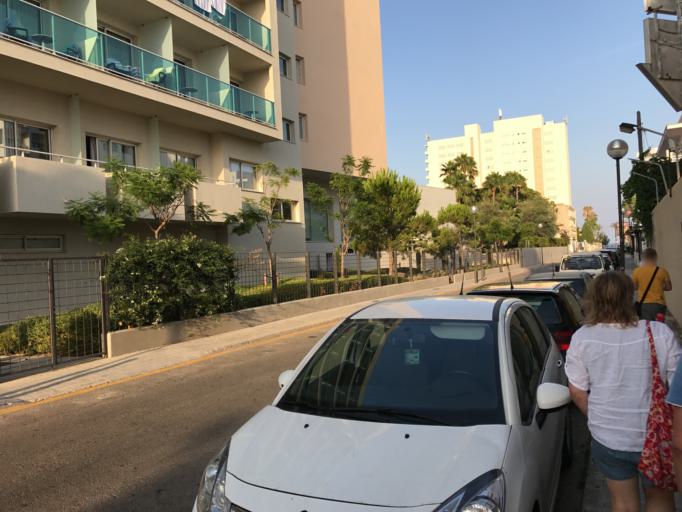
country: ES
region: Balearic Islands
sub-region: Illes Balears
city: Son Servera
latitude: 39.5969
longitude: 3.3805
